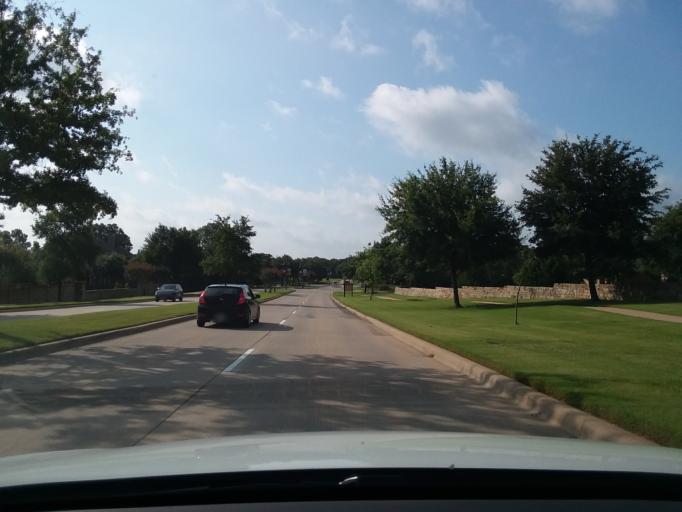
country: US
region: Texas
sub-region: Denton County
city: Bartonville
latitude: 33.0783
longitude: -97.1257
